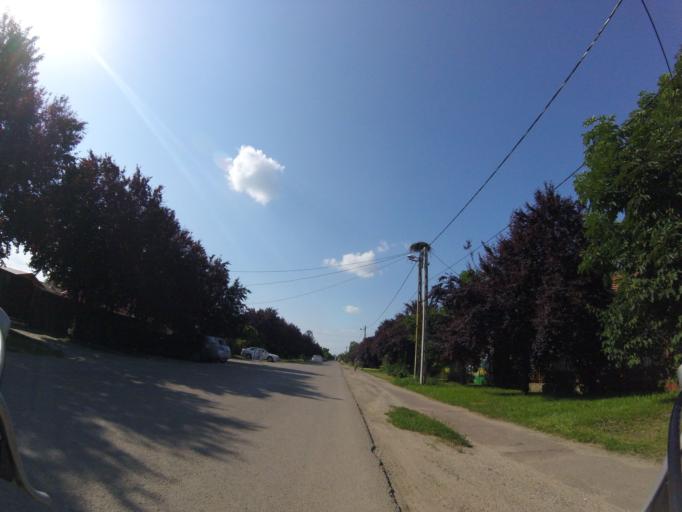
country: HU
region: Heves
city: Kiskore
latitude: 47.4976
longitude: 20.4936
